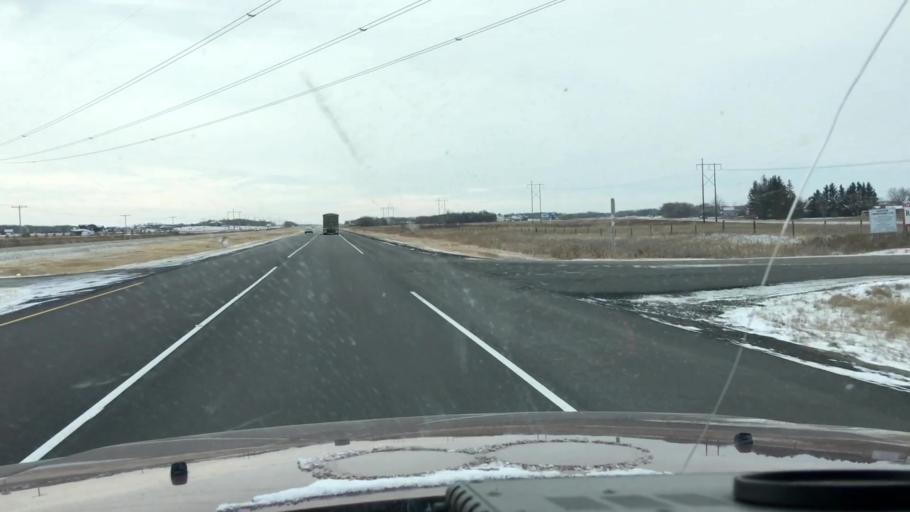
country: CA
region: Saskatchewan
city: Saskatoon
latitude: 51.9549
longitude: -106.5470
